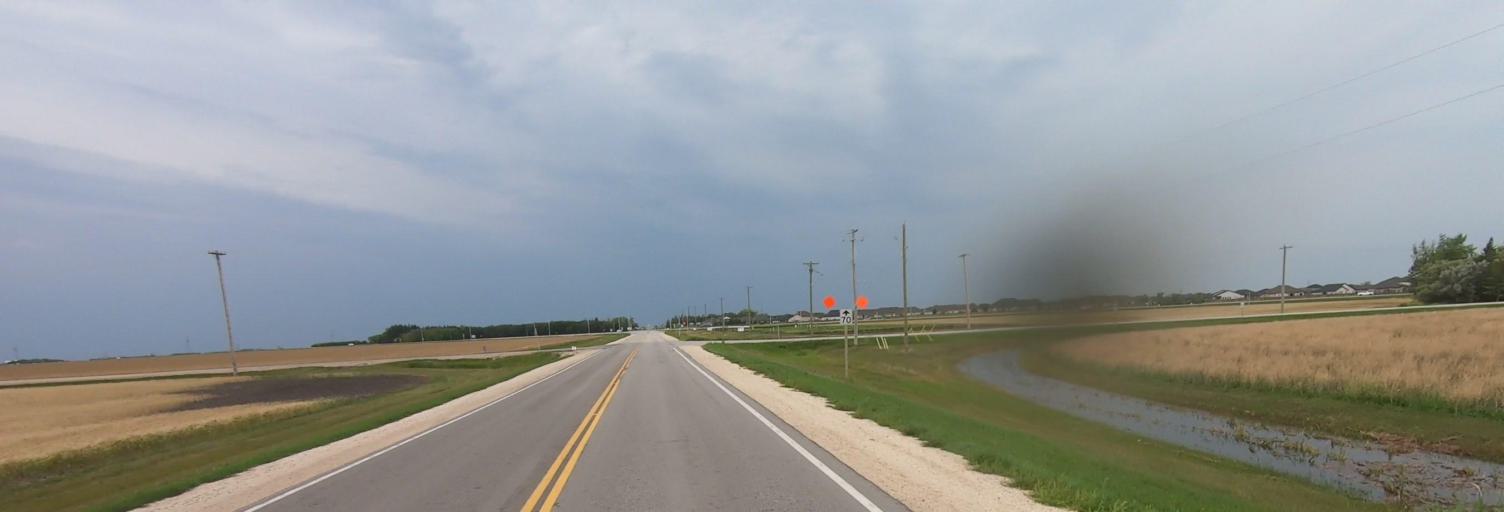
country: CA
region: Manitoba
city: Headingley
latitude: 49.7682
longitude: -97.3211
